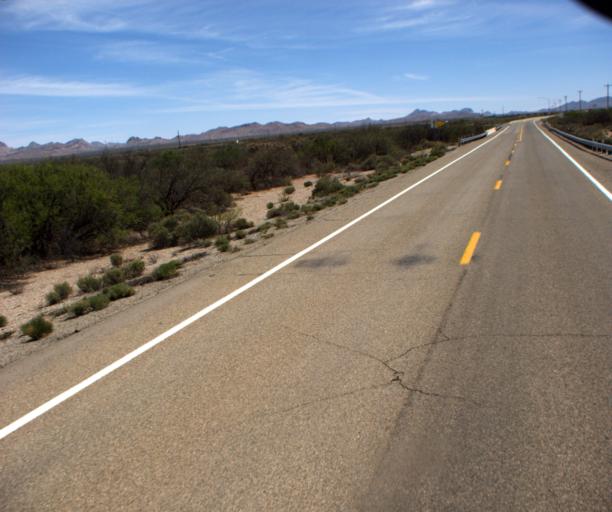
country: US
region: New Mexico
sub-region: Hidalgo County
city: Lordsburg
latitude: 32.2604
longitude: -109.2008
